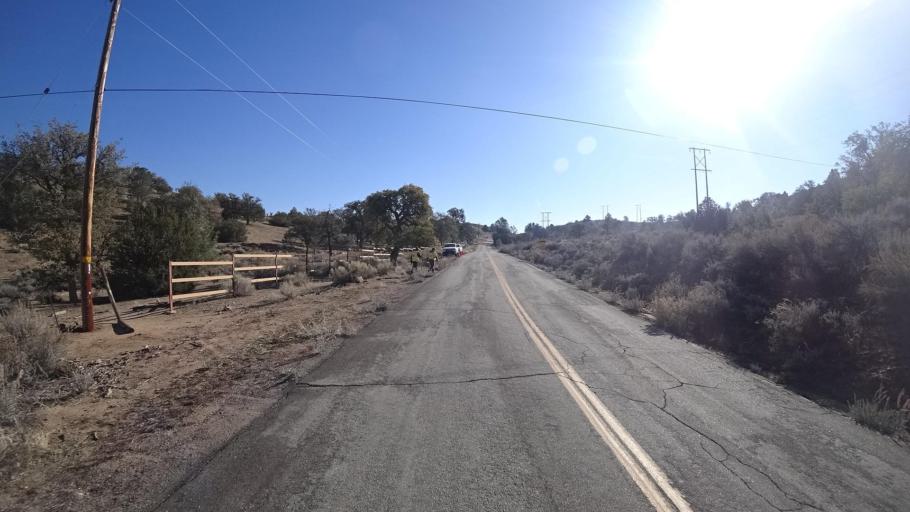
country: US
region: California
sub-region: Kern County
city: Bodfish
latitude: 35.3845
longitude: -118.4150
